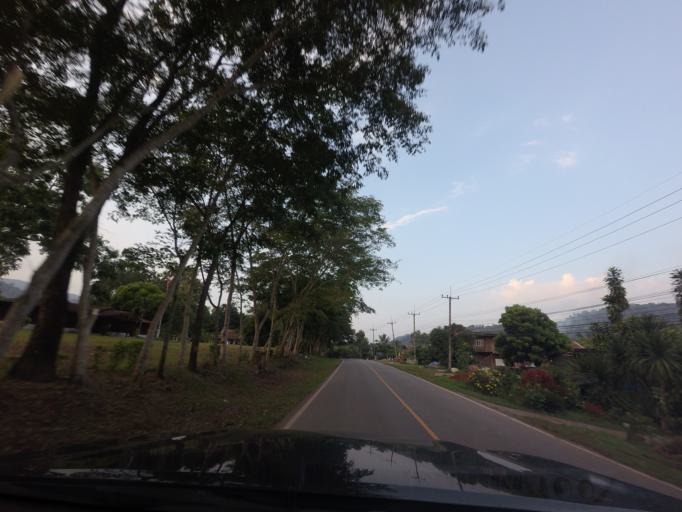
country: TH
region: Loei
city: Na Haeo
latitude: 17.4307
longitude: 101.0507
